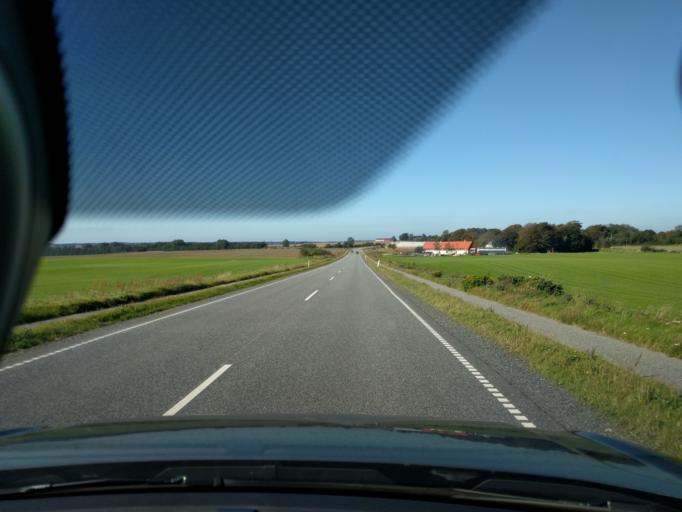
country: DK
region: North Denmark
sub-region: Vesthimmerland Kommune
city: Aars
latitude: 56.7429
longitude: 9.5950
